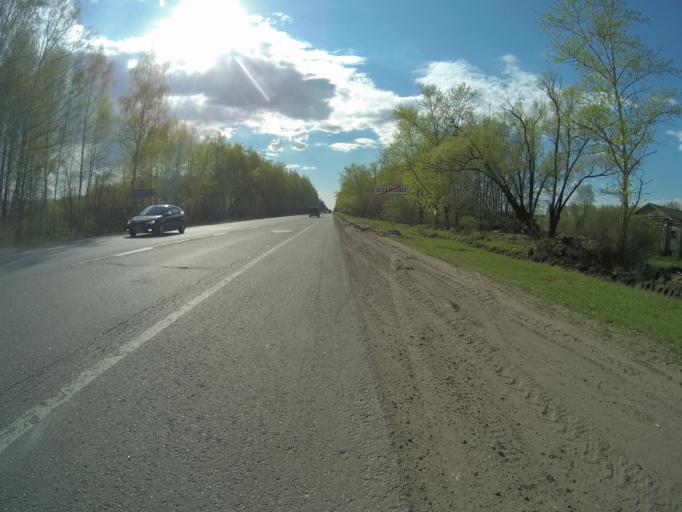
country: RU
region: Vladimir
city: Orgtrud
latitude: 56.2038
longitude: 40.7478
